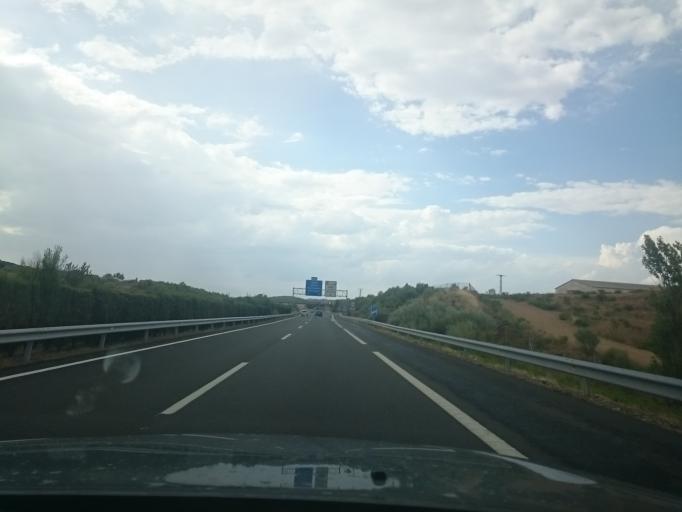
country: ES
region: Navarre
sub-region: Provincia de Navarra
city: Sartaguda
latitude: 42.3663
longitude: -2.0726
